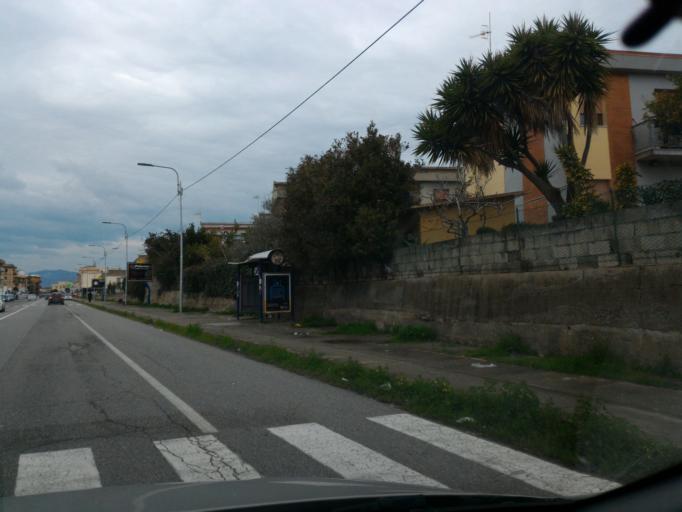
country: IT
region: Calabria
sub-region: Provincia di Catanzaro
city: Barone
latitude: 38.8332
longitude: 16.6327
